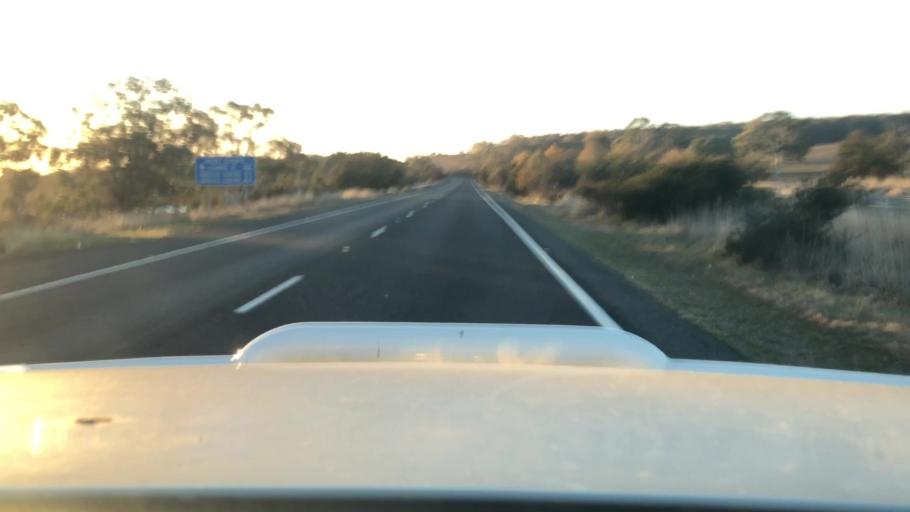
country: AU
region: New South Wales
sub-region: Goulburn Mulwaree
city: Goulburn
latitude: -34.7878
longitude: 149.6419
